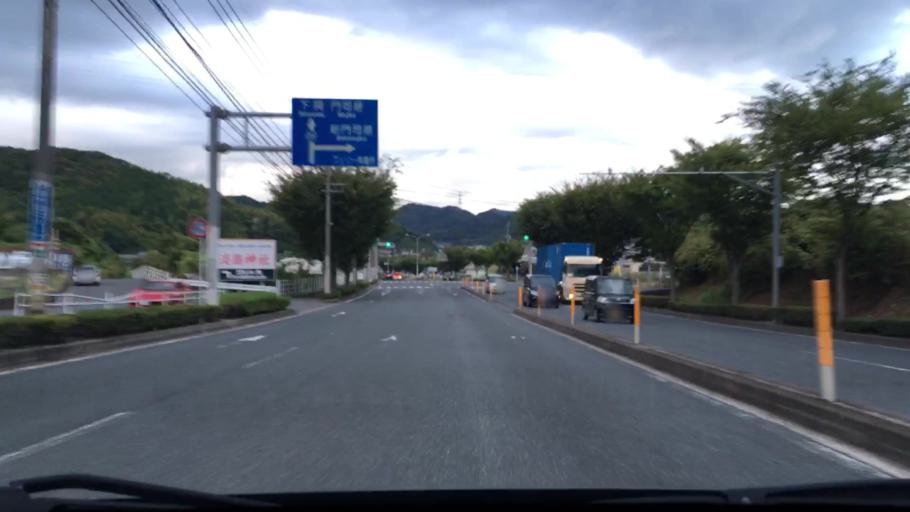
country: JP
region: Yamaguchi
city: Shimonoseki
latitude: 33.8868
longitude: 130.9780
